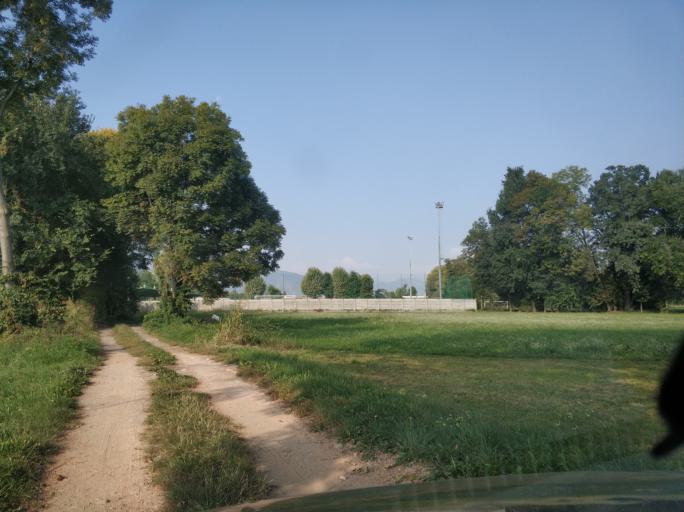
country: IT
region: Piedmont
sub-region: Provincia di Torino
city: Nole
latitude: 45.2460
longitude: 7.5813
